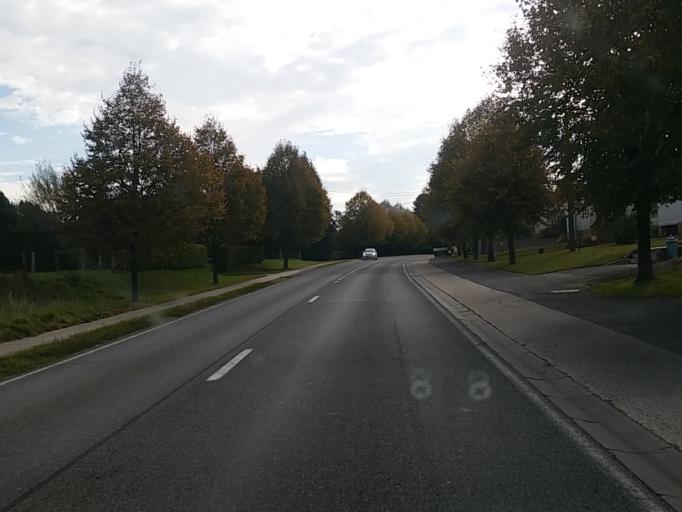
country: BE
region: Wallonia
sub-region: Province du Luxembourg
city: Tintigny
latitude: 49.6819
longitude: 5.5229
